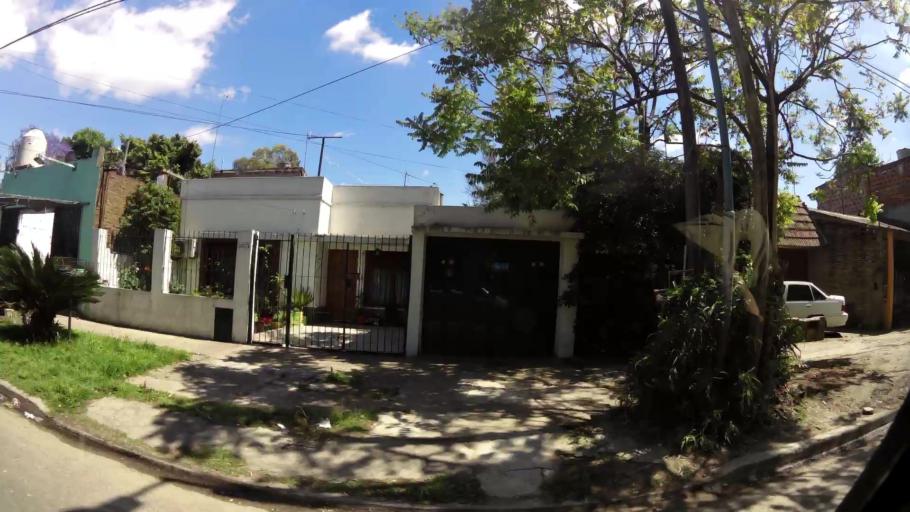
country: AR
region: Buenos Aires
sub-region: Partido de Lanus
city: Lanus
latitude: -34.6921
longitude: -58.4293
